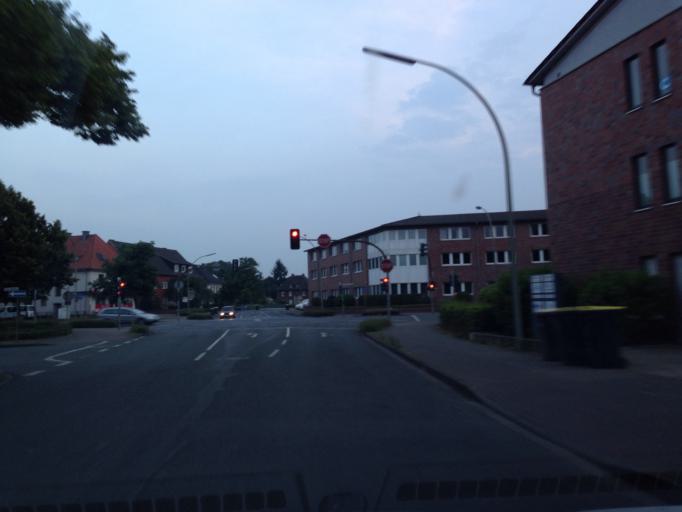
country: DE
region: North Rhine-Westphalia
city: Ludinghausen
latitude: 51.7684
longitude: 7.4440
